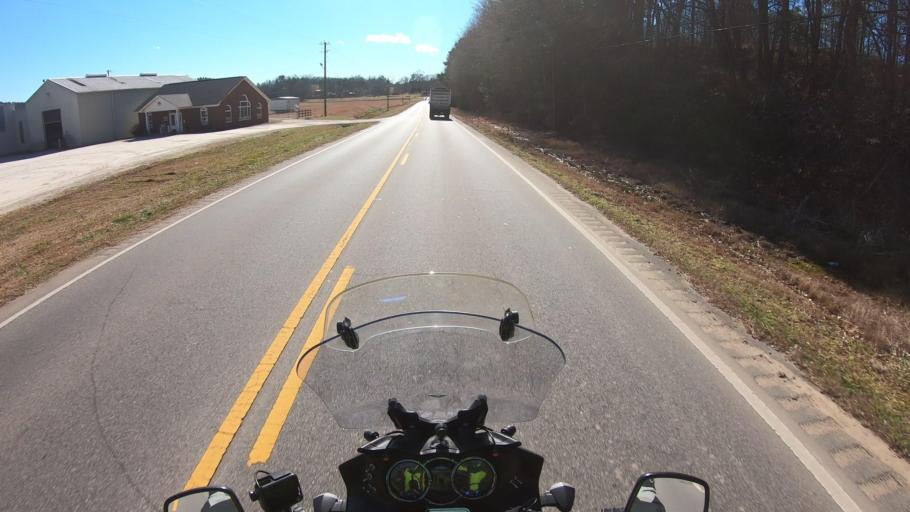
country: US
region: Alabama
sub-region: Cleburne County
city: Heflin
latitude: 33.5989
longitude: -85.6064
